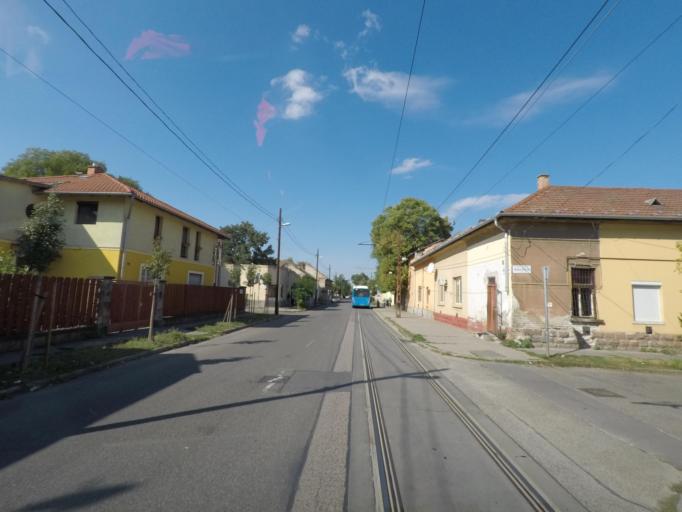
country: HU
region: Budapest
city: Budapest XX. keruelet
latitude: 47.4454
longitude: 19.1094
